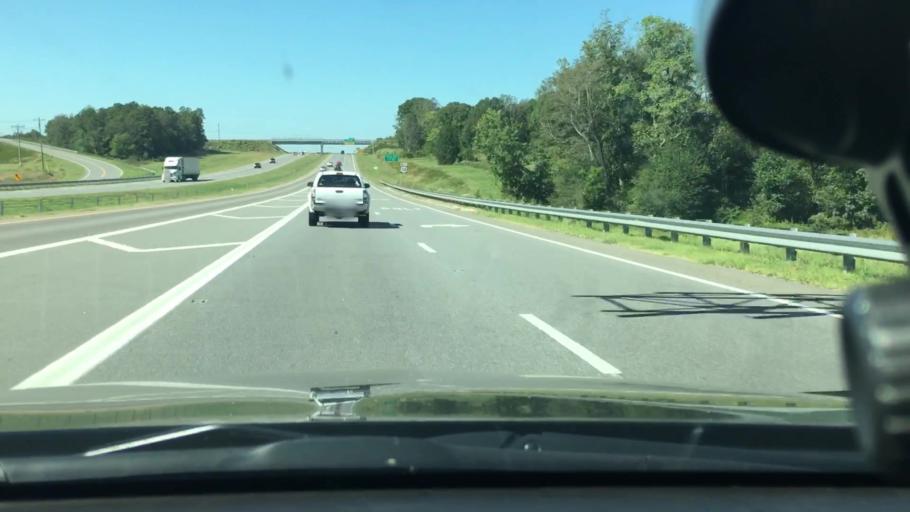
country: US
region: North Carolina
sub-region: Cleveland County
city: Boiling Springs
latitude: 35.2971
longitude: -81.6634
